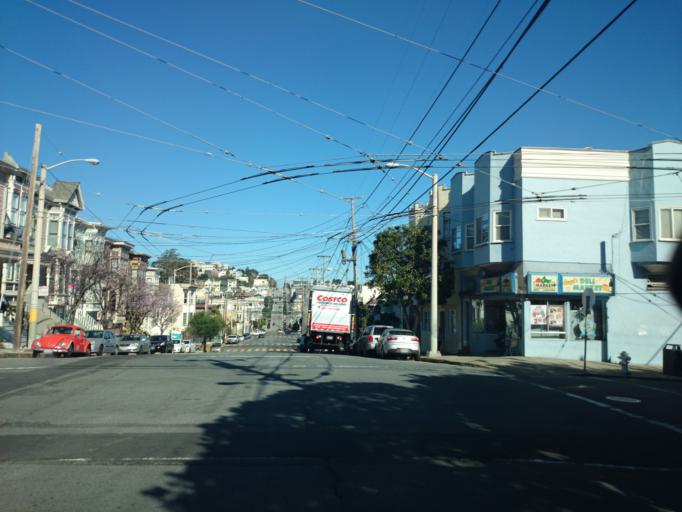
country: US
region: California
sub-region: San Francisco County
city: San Francisco
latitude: 37.7480
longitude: -122.4337
